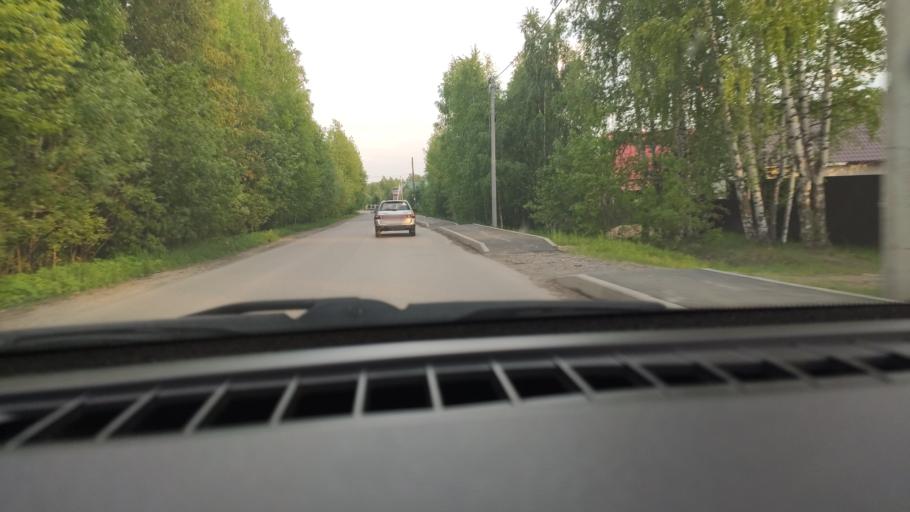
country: RU
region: Perm
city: Kondratovo
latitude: 58.0599
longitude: 56.0044
